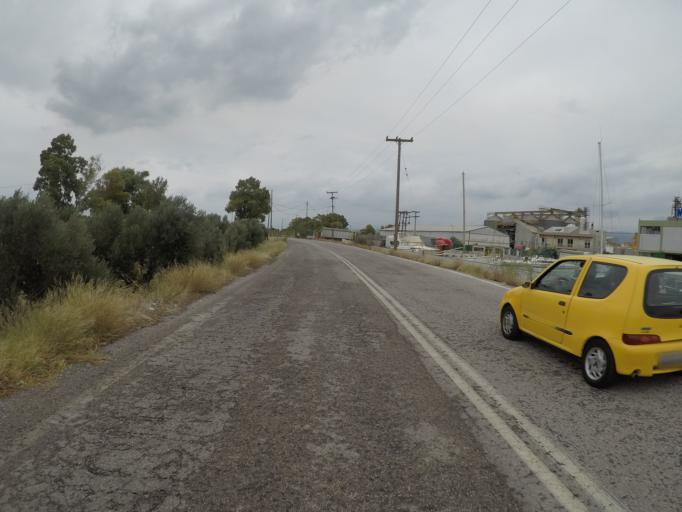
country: GR
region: Peloponnese
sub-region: Nomos Korinthias
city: Isthmia
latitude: 37.9220
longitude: 23.0229
